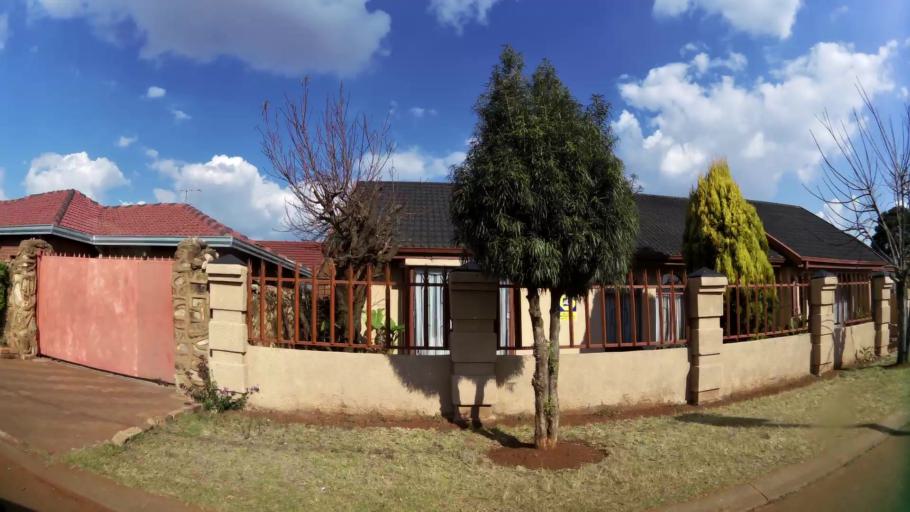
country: ZA
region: Gauteng
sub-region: City of Johannesburg Metropolitan Municipality
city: Soweto
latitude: -26.2223
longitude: 27.8619
